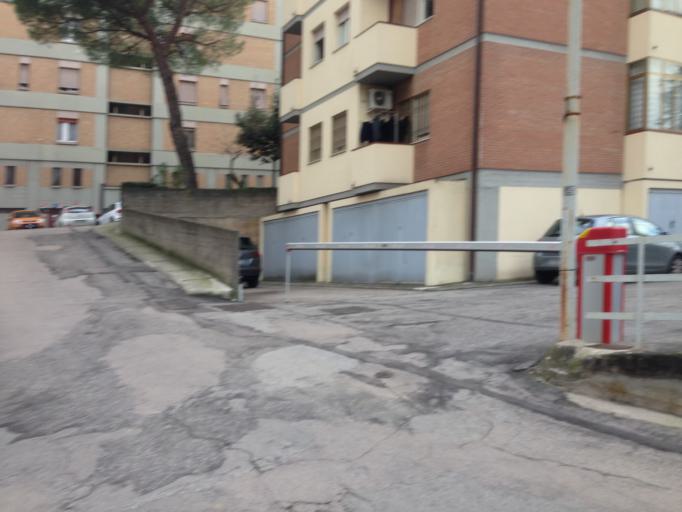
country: IT
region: Umbria
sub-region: Provincia di Perugia
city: Perugia
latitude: 43.1041
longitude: 12.3692
